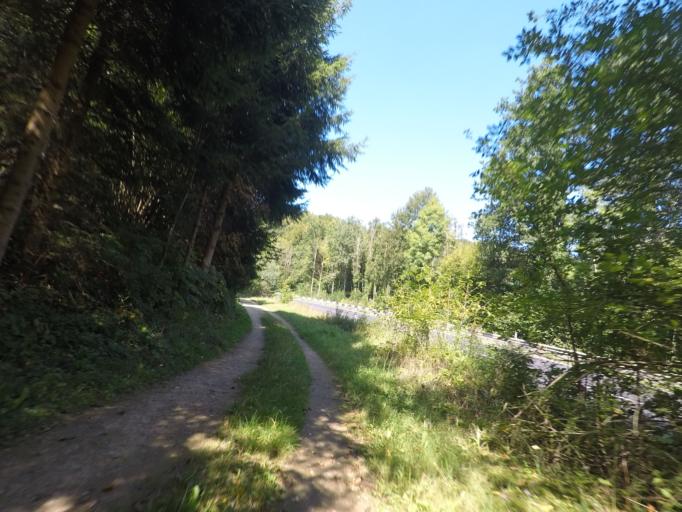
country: LU
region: Luxembourg
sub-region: Canton de Luxembourg
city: Strassen
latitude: 49.6313
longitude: 6.0899
